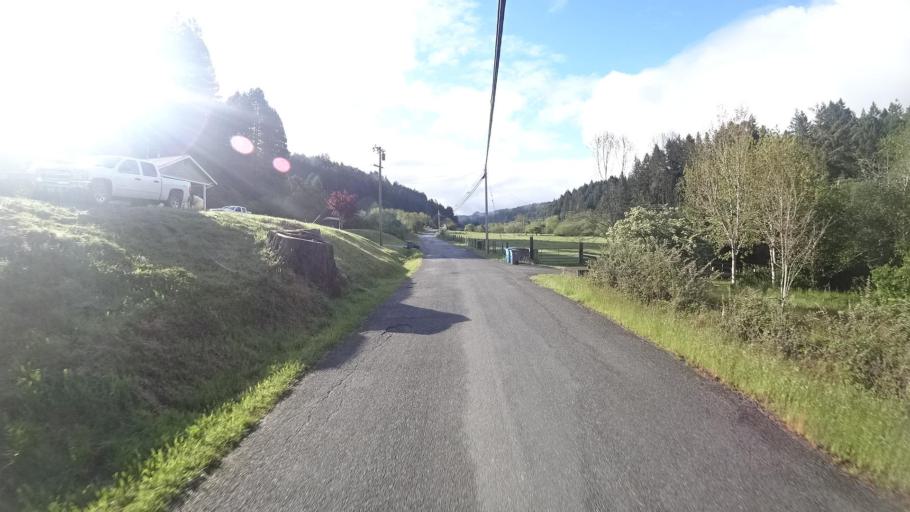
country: US
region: California
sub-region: Humboldt County
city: Arcata
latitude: 40.8961
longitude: -124.0445
